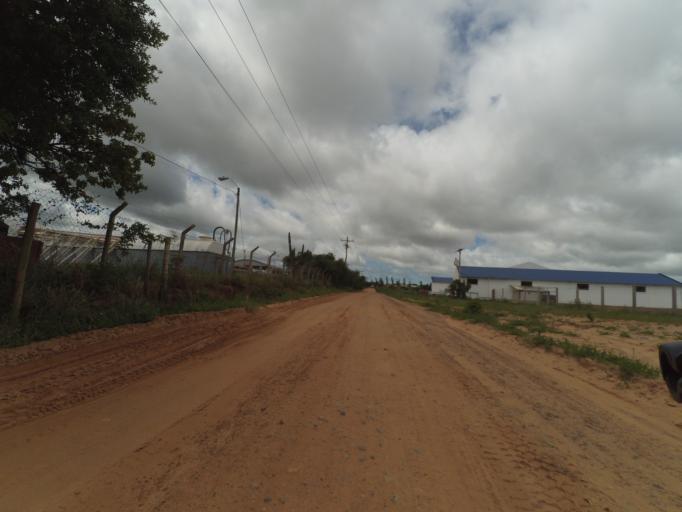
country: BO
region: Santa Cruz
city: Santa Rita
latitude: -17.9107
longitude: -63.2489
